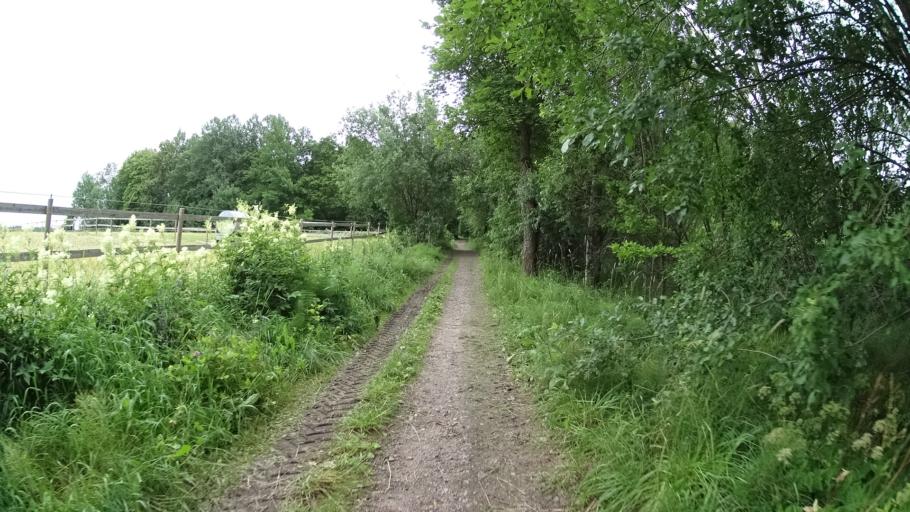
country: FI
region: Uusimaa
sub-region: Helsinki
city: Kauniainen
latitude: 60.2489
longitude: 24.7003
